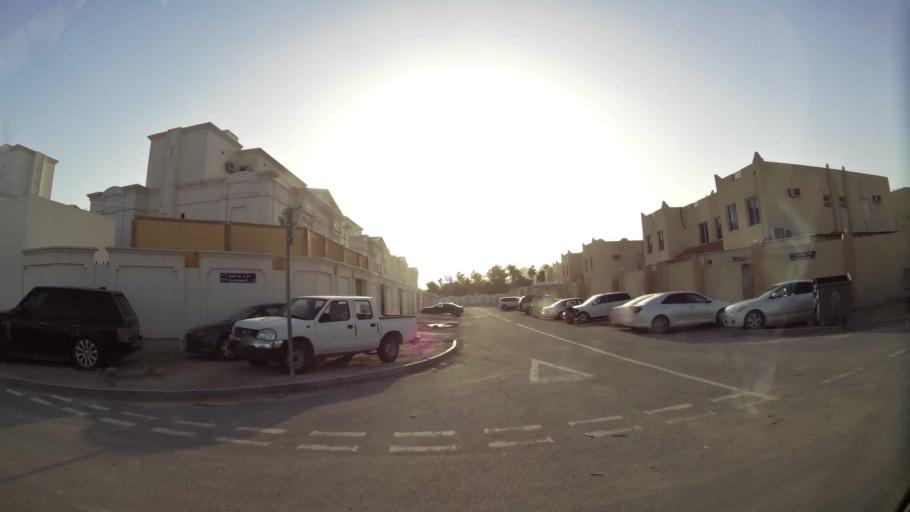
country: QA
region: Baladiyat ar Rayyan
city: Ar Rayyan
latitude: 25.3219
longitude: 51.4541
